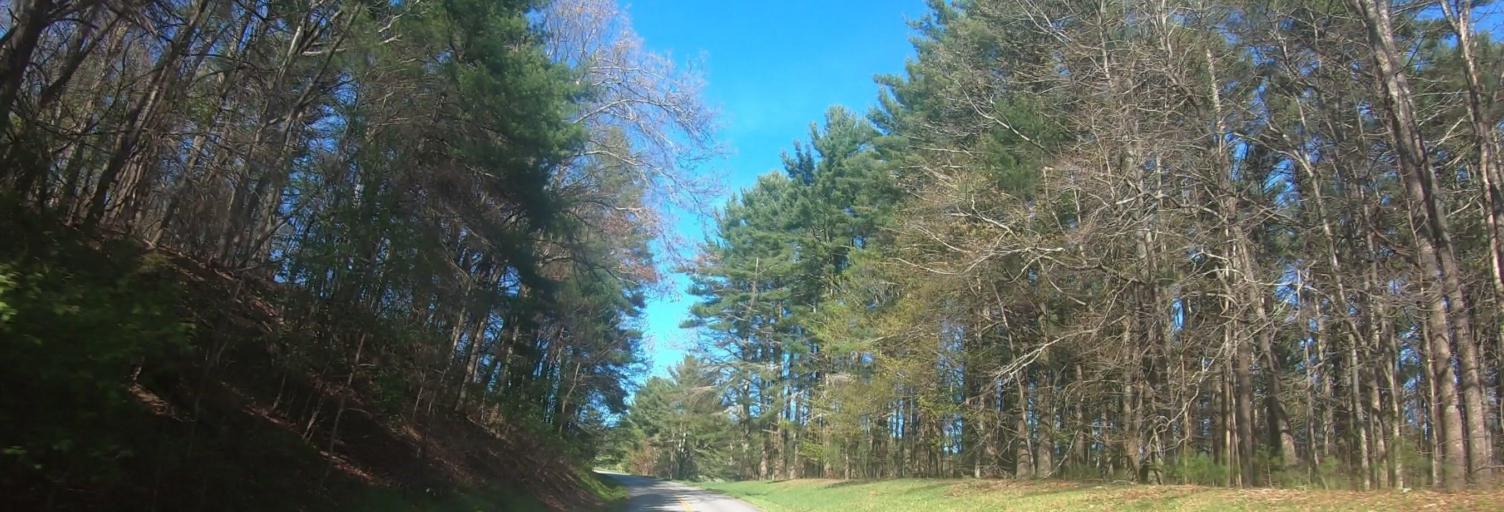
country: US
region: North Carolina
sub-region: Watauga County
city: Boone
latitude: 36.2293
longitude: -81.5424
